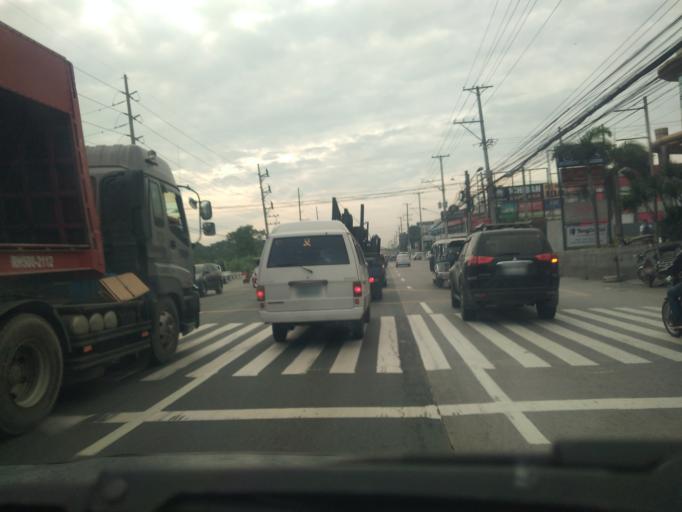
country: PH
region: Central Luzon
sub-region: Province of Pampanga
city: Bulaon
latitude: 15.0595
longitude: 120.6565
